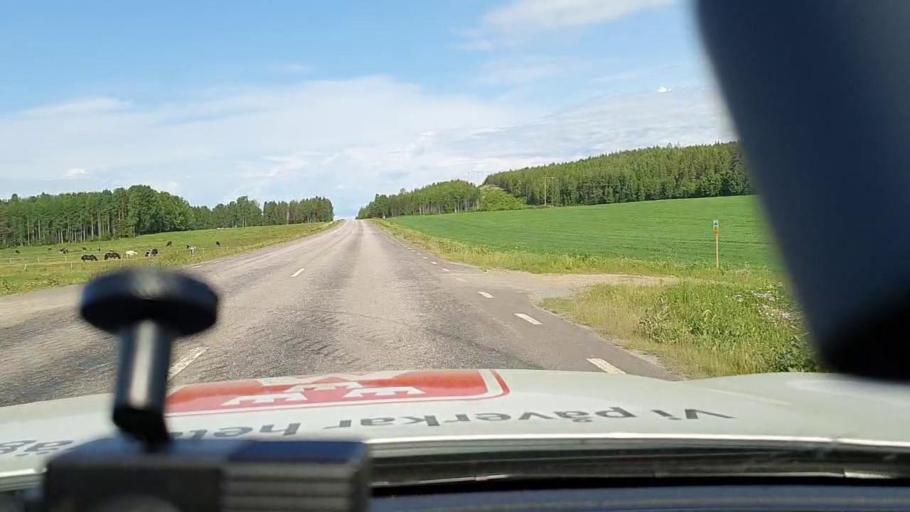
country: SE
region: Norrbotten
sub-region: Bodens Kommun
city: Boden
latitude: 65.9123
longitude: 21.3458
